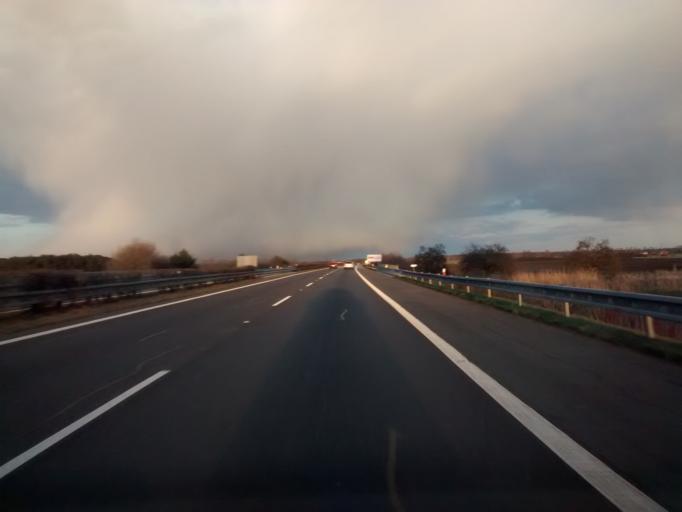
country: CZ
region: Central Bohemia
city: Pecky
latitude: 50.1232
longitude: 15.0397
